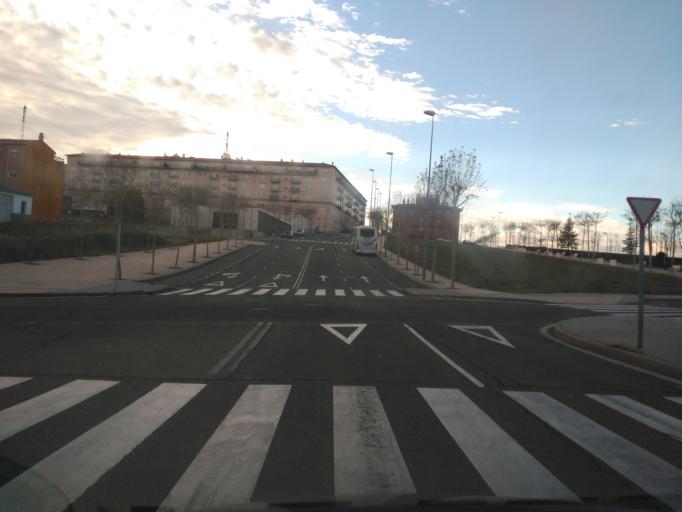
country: ES
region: Castille and Leon
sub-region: Provincia de Salamanca
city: Salamanca
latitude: 40.9810
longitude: -5.6691
